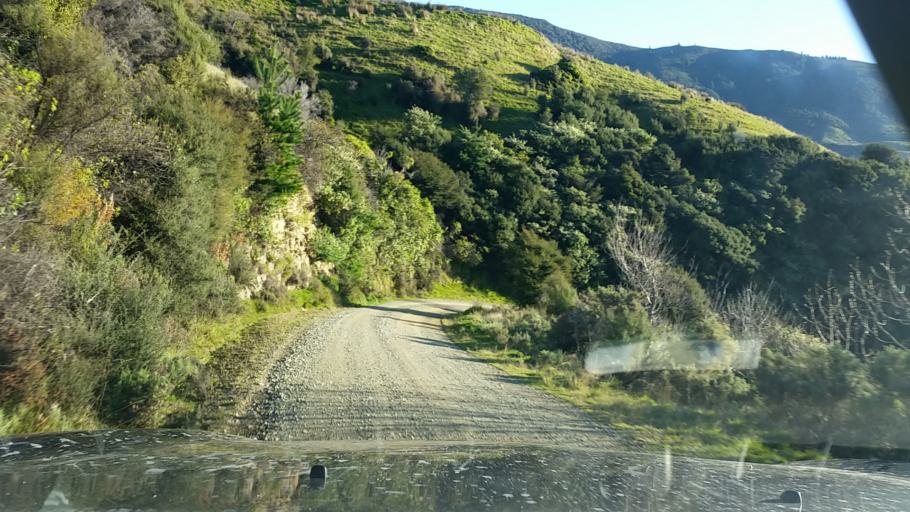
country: NZ
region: Marlborough
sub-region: Marlborough District
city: Picton
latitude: -41.0209
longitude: 174.1419
